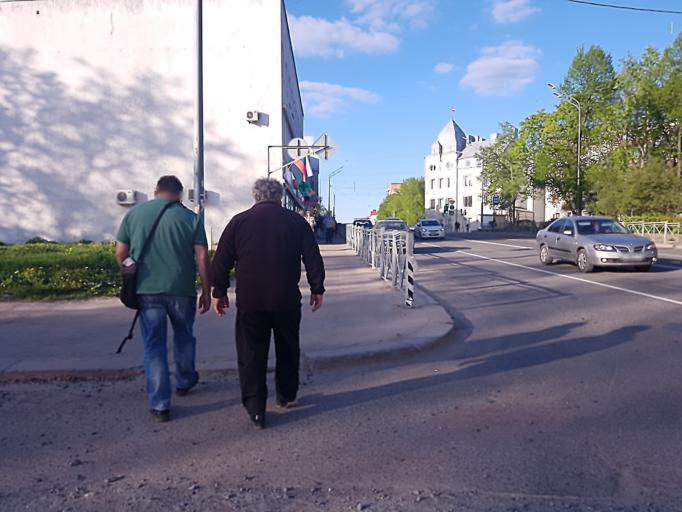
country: RU
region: Republic of Karelia
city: Sortavala
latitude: 61.7017
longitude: 30.6882
